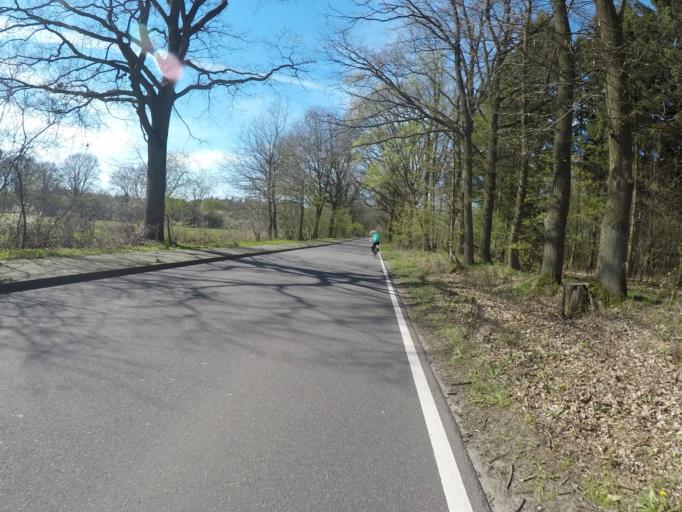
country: DE
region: Schleswig-Holstein
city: Tangstedt
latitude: 53.7121
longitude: 10.0834
